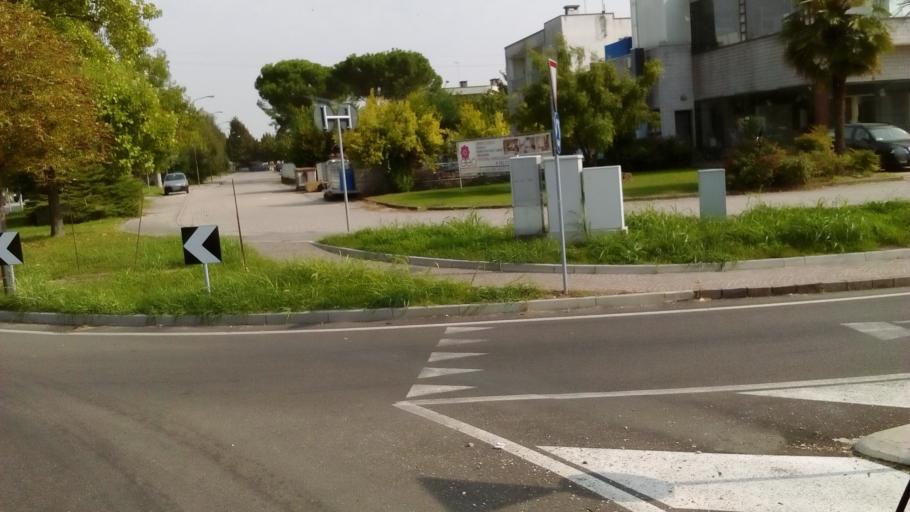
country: IT
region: Veneto
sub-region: Provincia di Padova
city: Tribano
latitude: 45.2145
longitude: 11.8336
